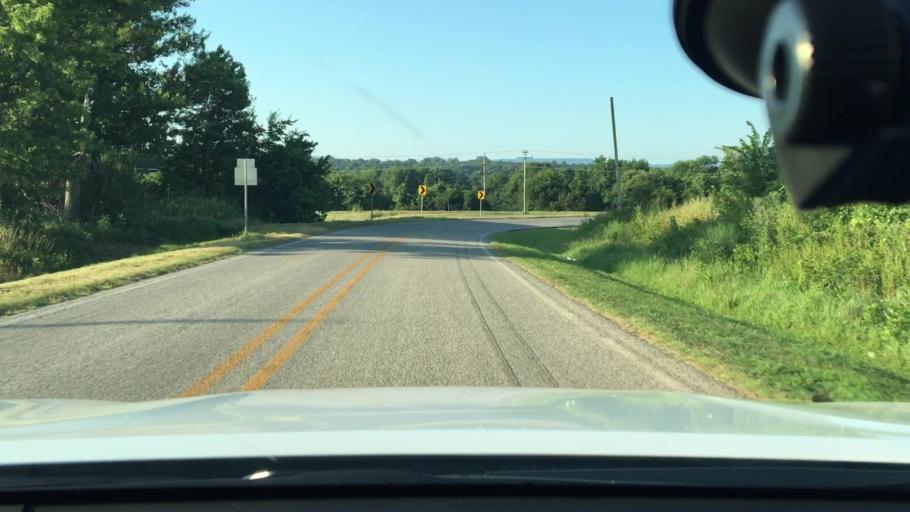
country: US
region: Arkansas
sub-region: Johnson County
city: Coal Hill
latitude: 35.3383
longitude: -93.6037
